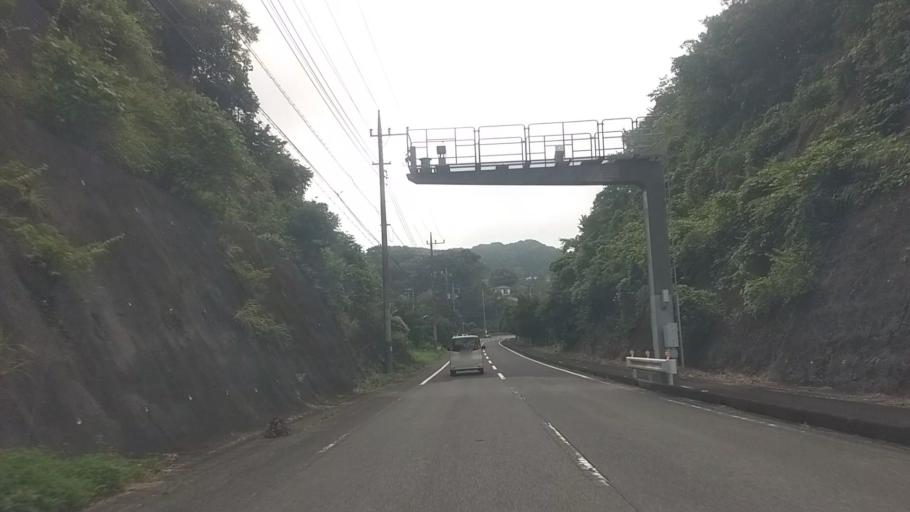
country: JP
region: Chiba
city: Kawaguchi
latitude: 35.2394
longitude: 140.1669
